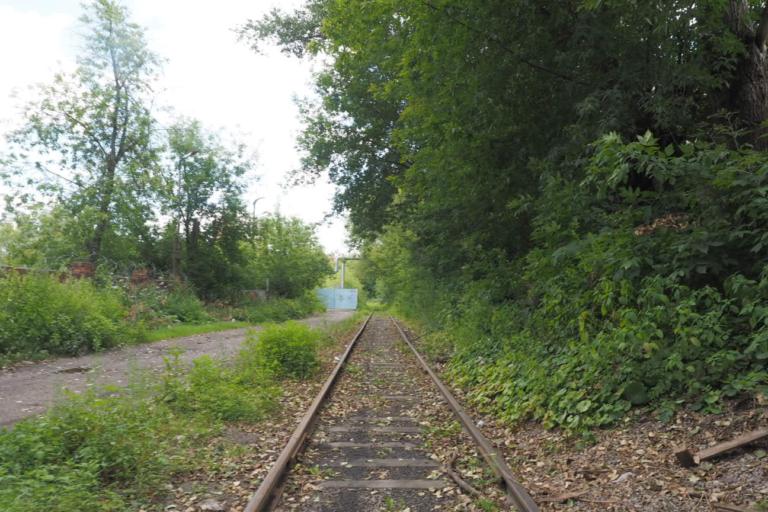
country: RU
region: Moskovskaya
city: Bogorodskoye
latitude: 55.7877
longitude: 37.7177
